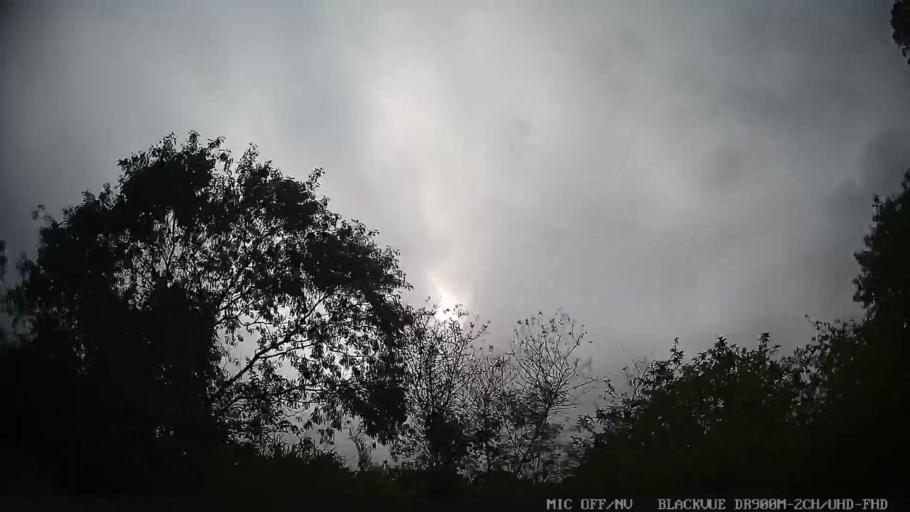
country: BR
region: Sao Paulo
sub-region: Osasco
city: Osasco
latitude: -23.4799
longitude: -46.7327
